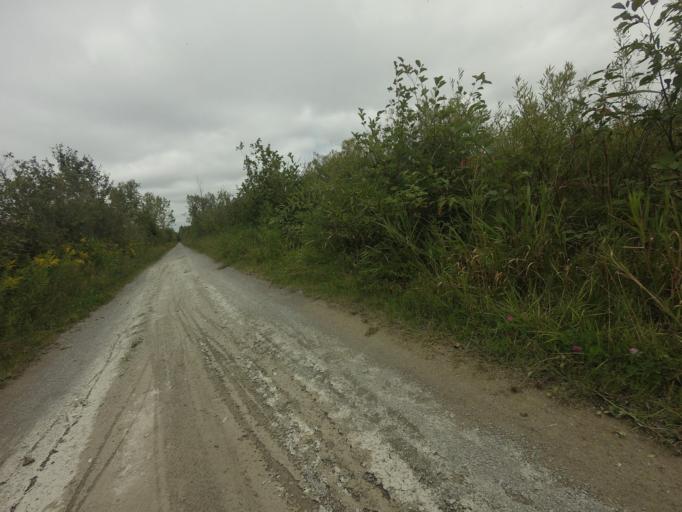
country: CA
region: Ontario
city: Uxbridge
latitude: 44.2407
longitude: -79.0443
